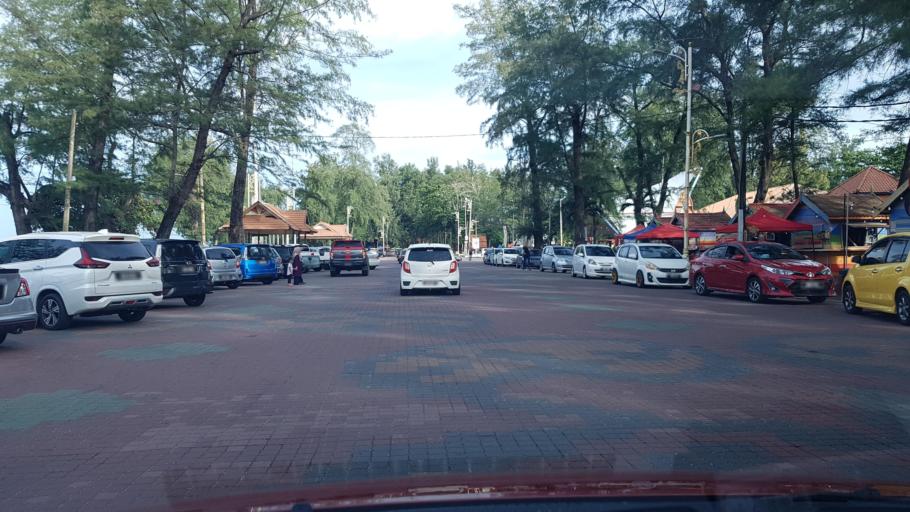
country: MY
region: Terengganu
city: Kuala Terengganu
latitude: 5.3233
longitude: 103.1545
